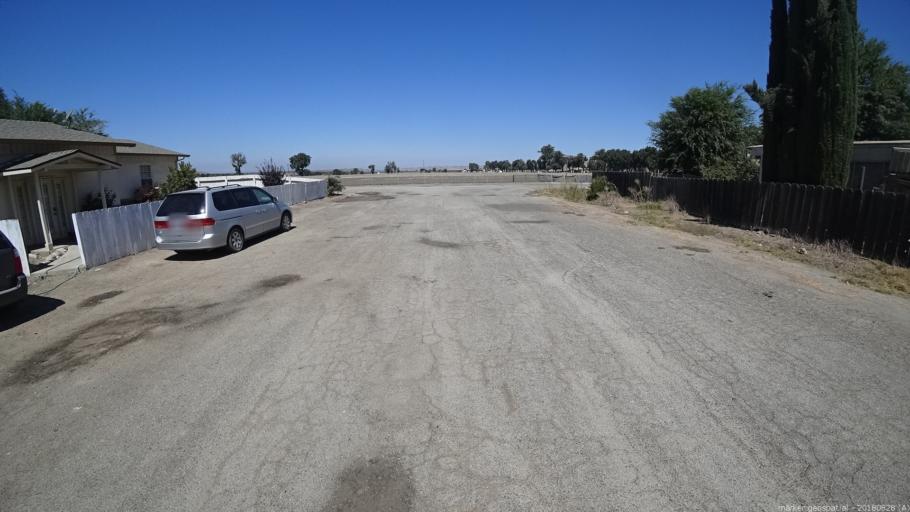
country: US
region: California
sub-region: Monterey County
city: King City
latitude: 36.0207
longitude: -120.9070
